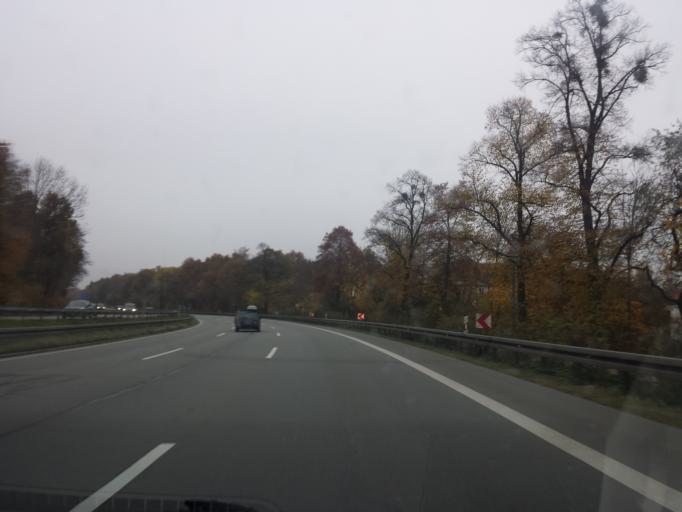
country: DE
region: Bavaria
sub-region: Upper Bavaria
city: Neuried
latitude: 48.0952
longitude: 11.4882
